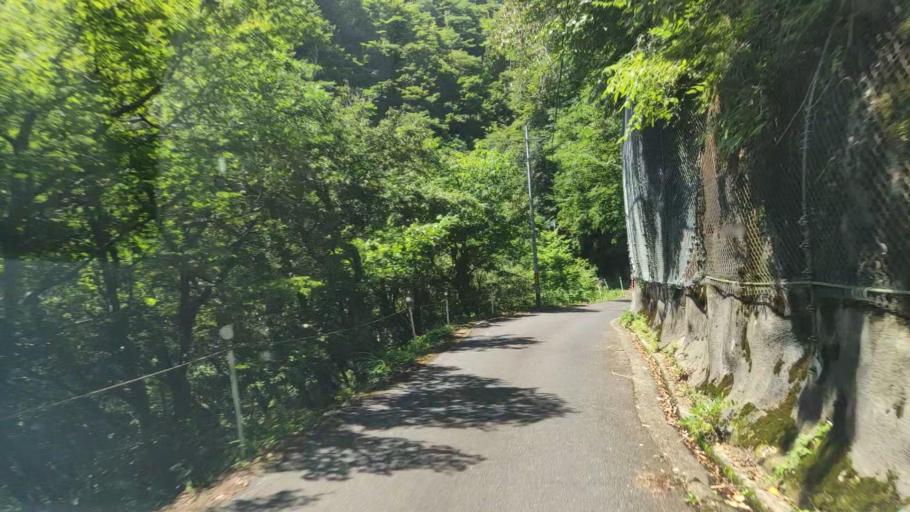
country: JP
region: Gifu
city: Godo
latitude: 35.6940
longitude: 136.5725
